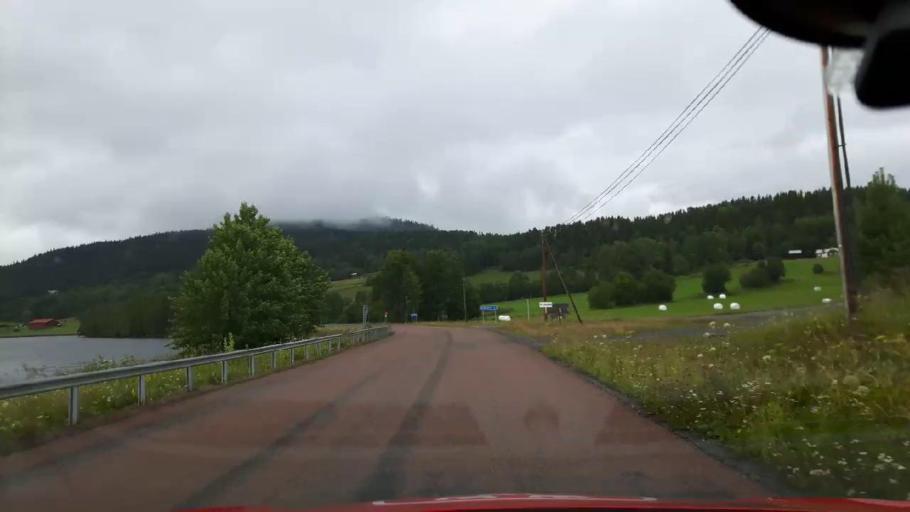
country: SE
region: Jaemtland
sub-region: Krokoms Kommun
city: Valla
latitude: 63.3780
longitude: 14.0157
